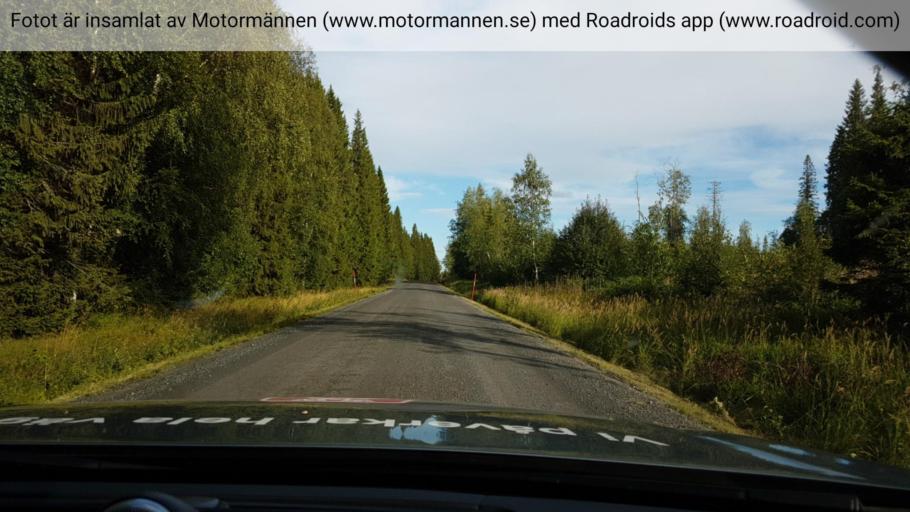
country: SE
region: Jaemtland
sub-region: Stroemsunds Kommun
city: Stroemsund
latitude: 64.1323
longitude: 15.7830
